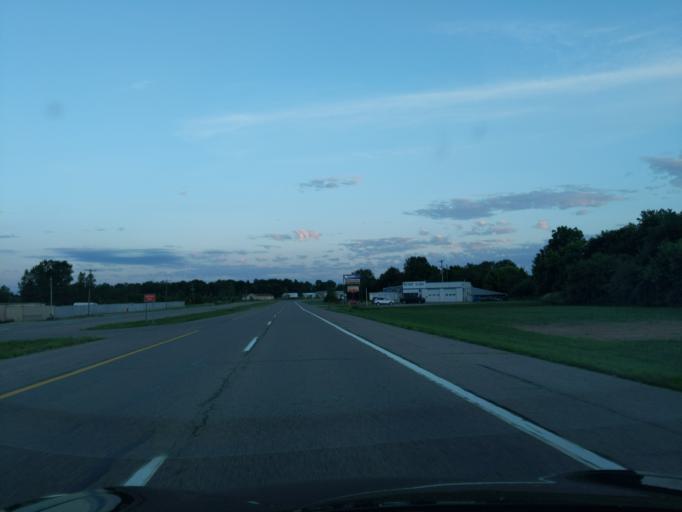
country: US
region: Michigan
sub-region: Clinton County
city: Saint Johns
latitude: 43.0120
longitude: -84.5553
